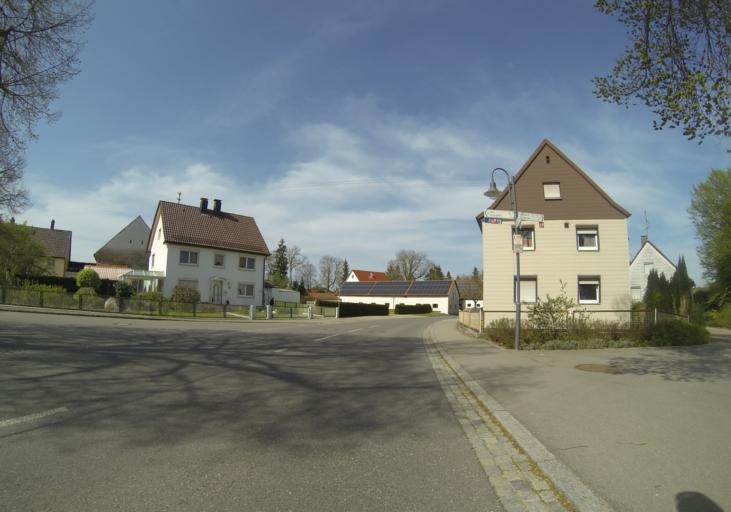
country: DE
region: Baden-Wuerttemberg
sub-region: Tuebingen Region
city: Achstetten
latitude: 48.2463
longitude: 9.9062
